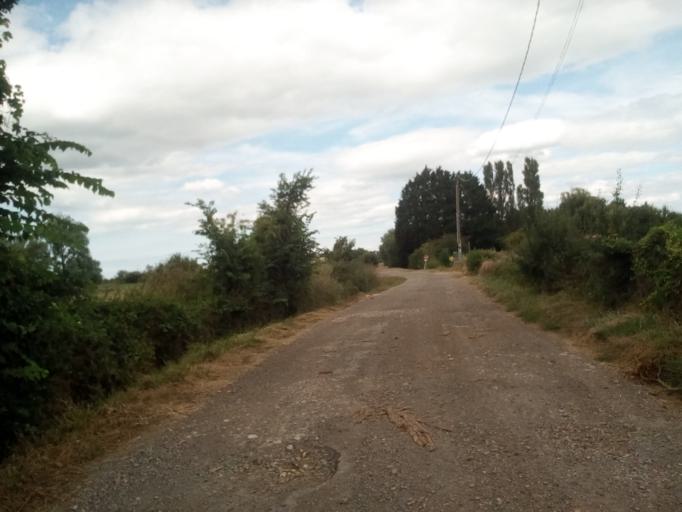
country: FR
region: Lower Normandy
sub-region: Departement du Calvados
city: Troarn
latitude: 49.1733
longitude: -0.1659
